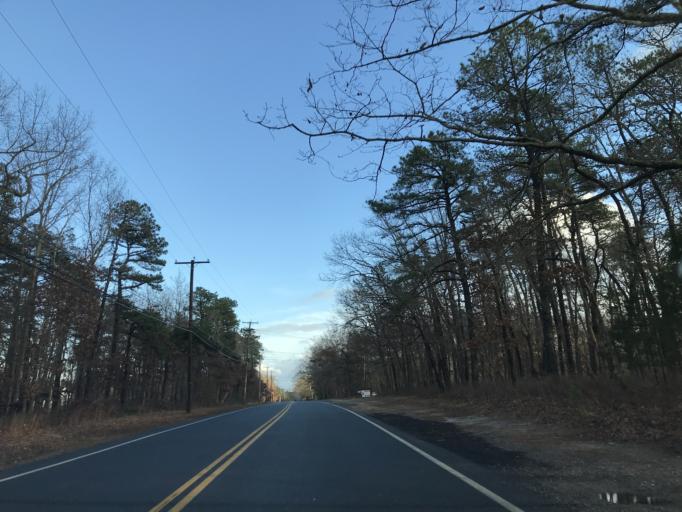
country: US
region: New Jersey
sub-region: Ocean County
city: Waretown
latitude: 39.7947
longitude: -74.2303
